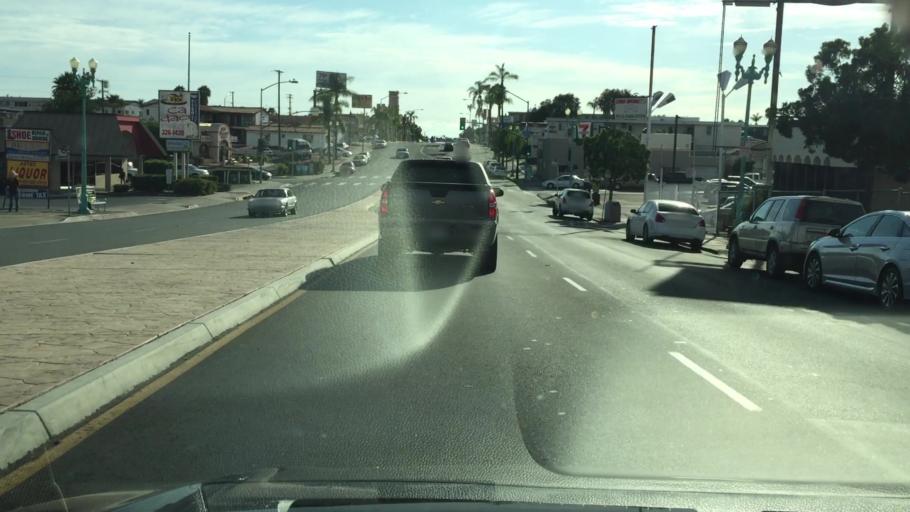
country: US
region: California
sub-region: San Diego County
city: Lemon Grove
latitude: 32.7574
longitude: -117.0826
